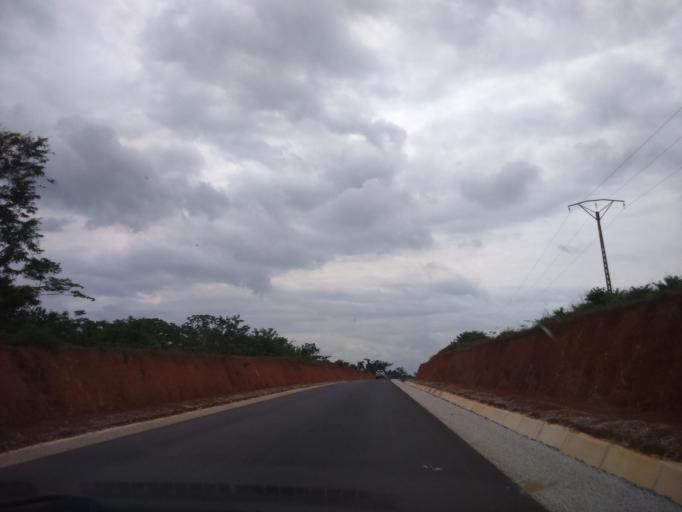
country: CI
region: Lagunes
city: Akoupe
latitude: 6.3309
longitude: -3.8447
